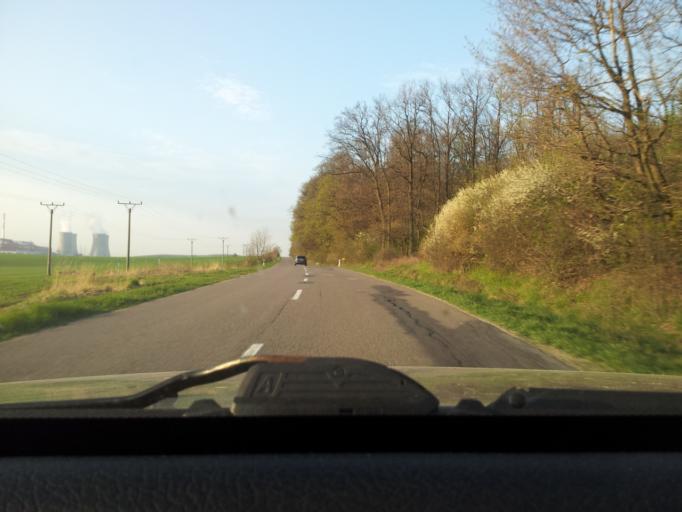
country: SK
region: Nitriansky
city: Tlmace
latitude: 48.2809
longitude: 18.4480
